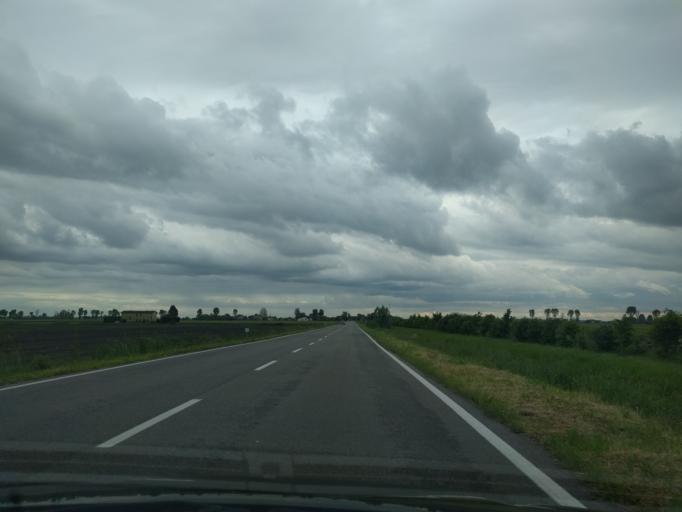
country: IT
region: Veneto
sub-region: Provincia di Rovigo
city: Buso
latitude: 45.0827
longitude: 11.8528
